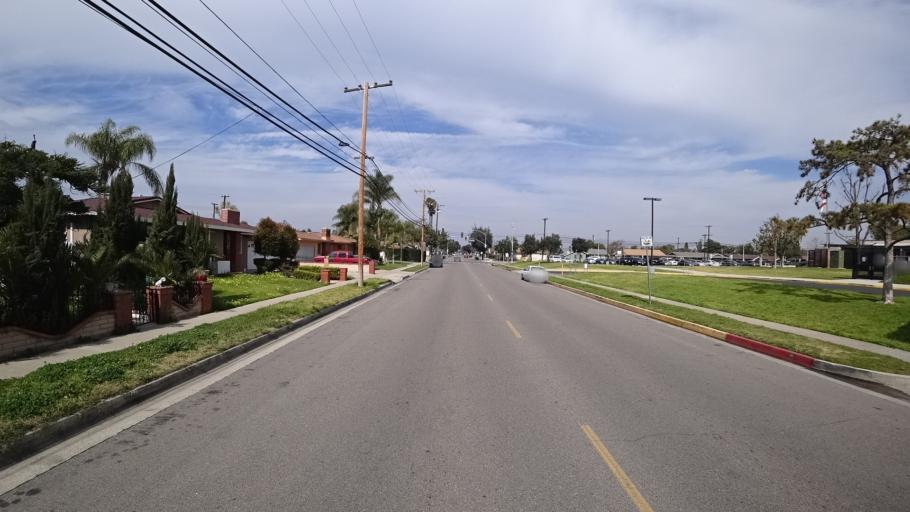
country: US
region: California
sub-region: Orange County
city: Garden Grove
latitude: 33.8096
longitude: -117.9502
